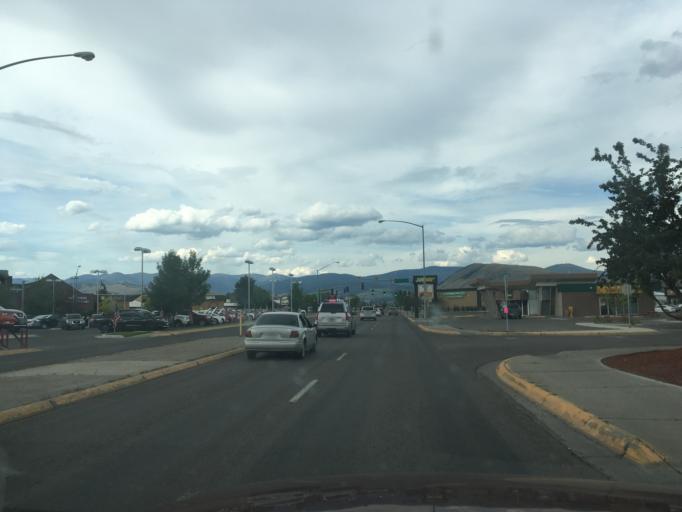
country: US
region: Montana
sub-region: Missoula County
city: Orchard Homes
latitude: 46.8451
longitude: -114.0234
